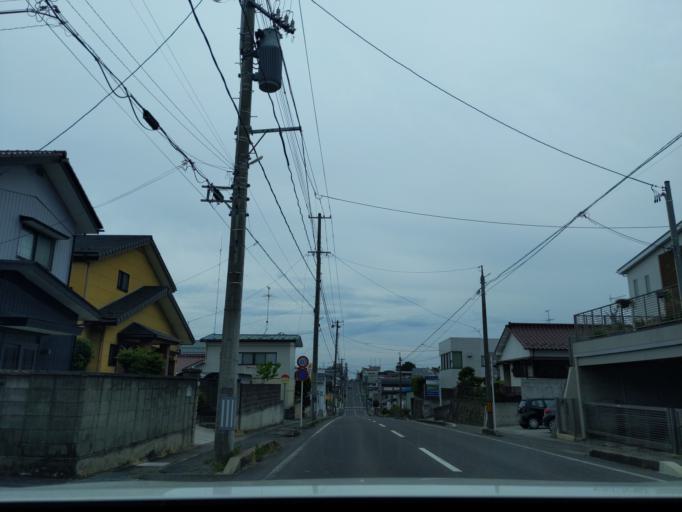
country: JP
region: Fukushima
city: Koriyama
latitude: 37.3843
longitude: 140.3697
